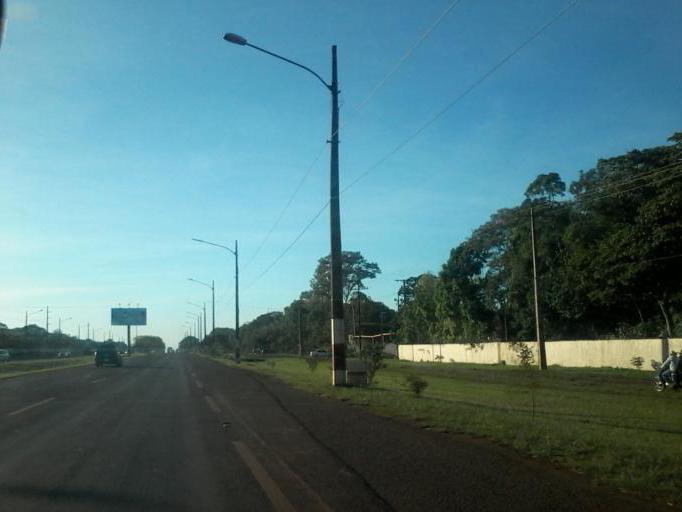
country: PY
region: Alto Parana
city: Ciudad del Este
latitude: -25.4394
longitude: -54.6346
